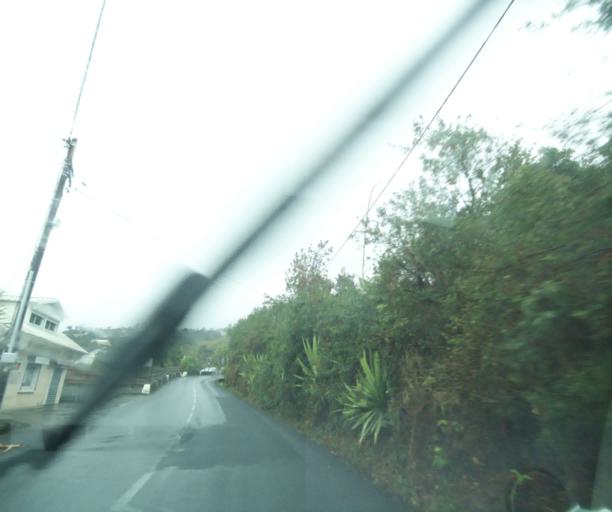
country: RE
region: Reunion
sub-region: Reunion
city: Saint-Paul
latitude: -21.0211
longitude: 55.2961
